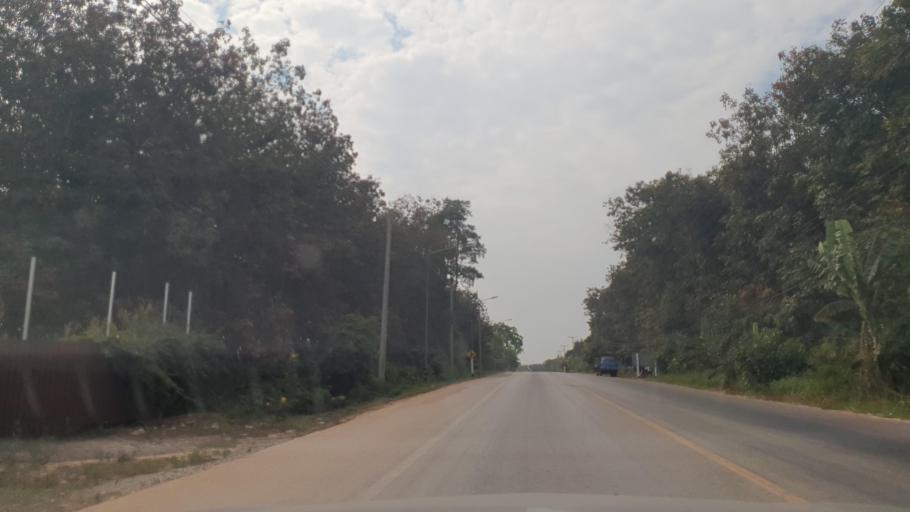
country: TH
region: Changwat Bueng Kan
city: Si Wilai
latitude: 18.3038
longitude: 103.8083
